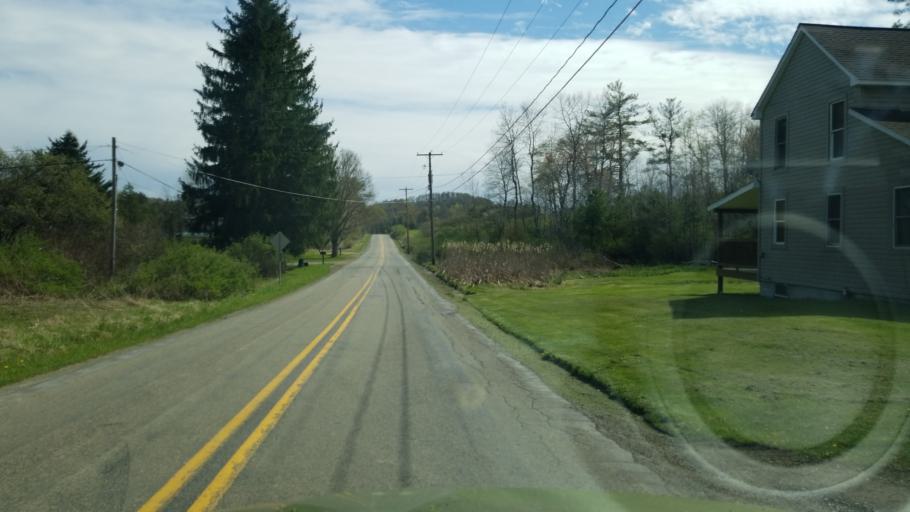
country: US
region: Pennsylvania
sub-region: Jefferson County
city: Brockway
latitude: 41.2294
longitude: -78.8511
